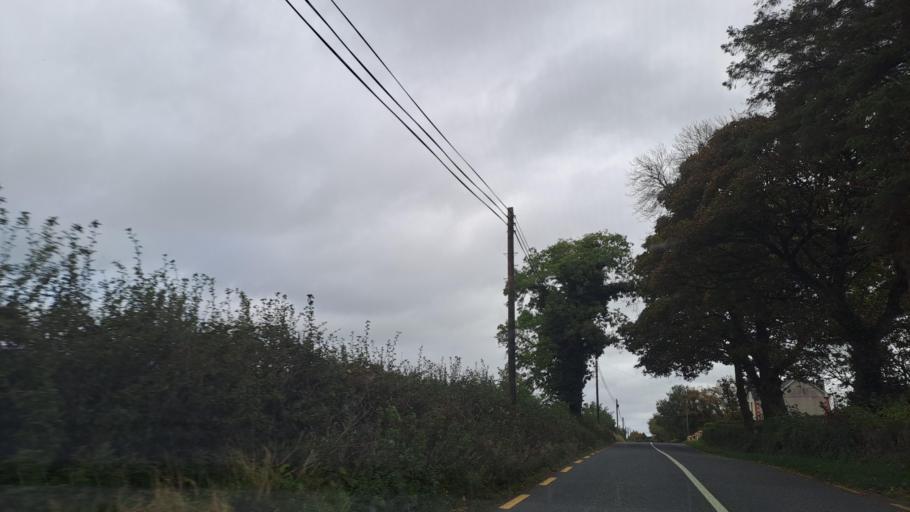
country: IE
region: Ulster
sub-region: An Cabhan
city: Kingscourt
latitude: 53.9100
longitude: -6.8276
